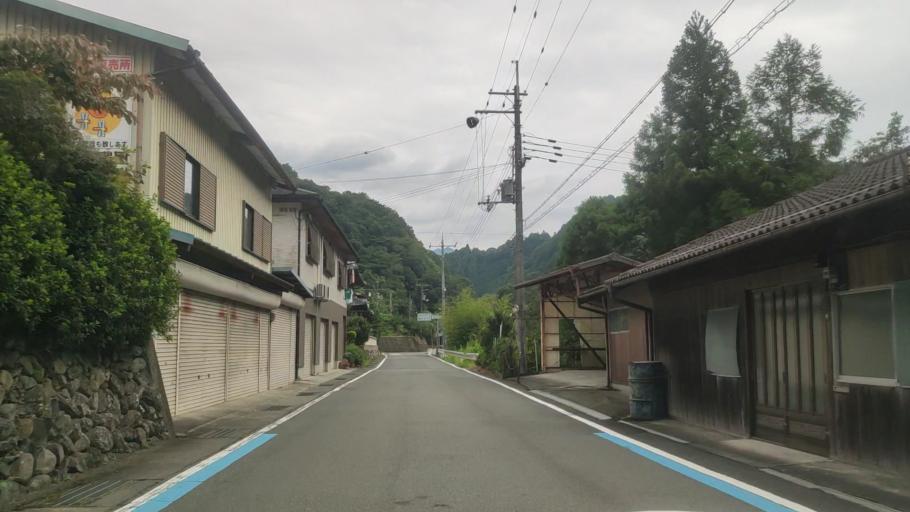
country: JP
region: Wakayama
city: Hashimoto
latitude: 34.2819
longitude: 135.5618
